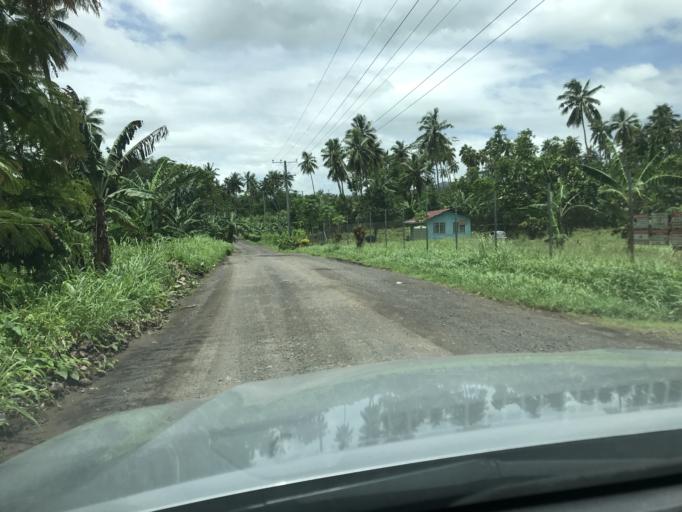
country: WS
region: Tuamasaga
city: Afenga
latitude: -13.8217
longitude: -171.8832
